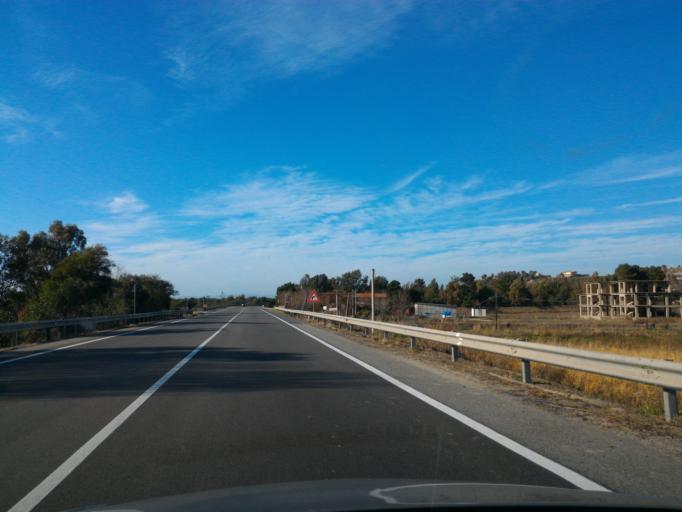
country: IT
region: Calabria
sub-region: Provincia di Crotone
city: Le Castella
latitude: 38.9406
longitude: 16.9758
